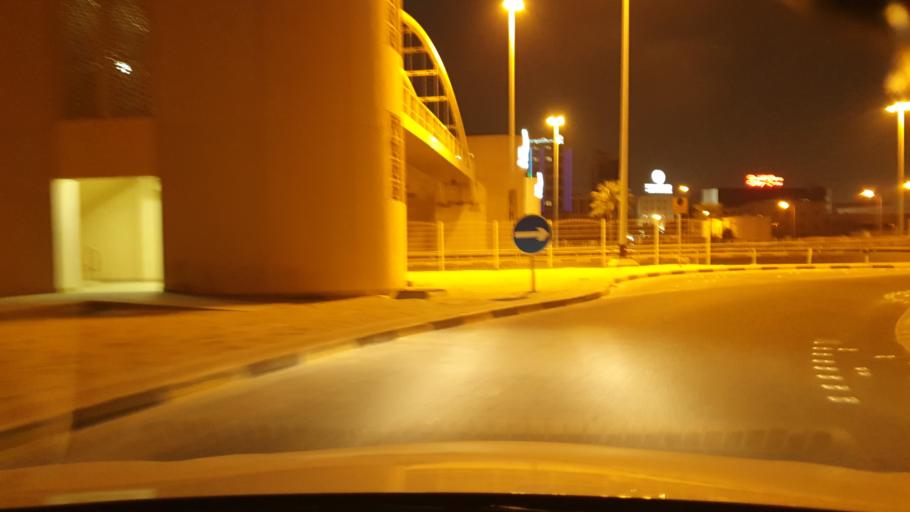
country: BH
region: Manama
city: Manama
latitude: 26.2359
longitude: 50.5721
